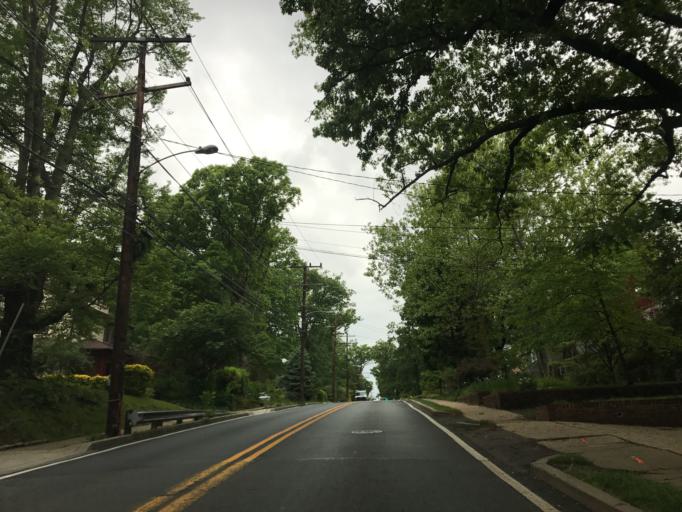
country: US
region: Maryland
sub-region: Montgomery County
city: Takoma Park
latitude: 38.9838
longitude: -77.0170
